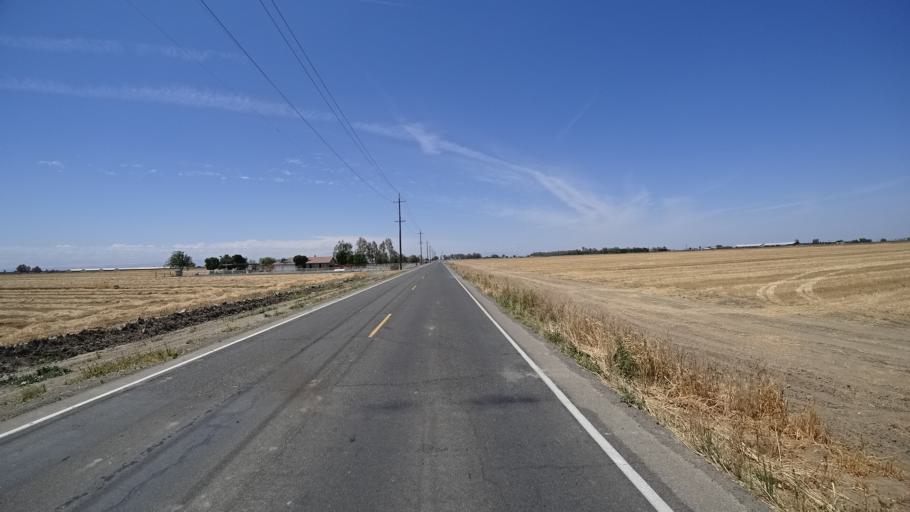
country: US
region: California
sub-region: Kings County
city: Lemoore
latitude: 36.2403
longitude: -119.7888
